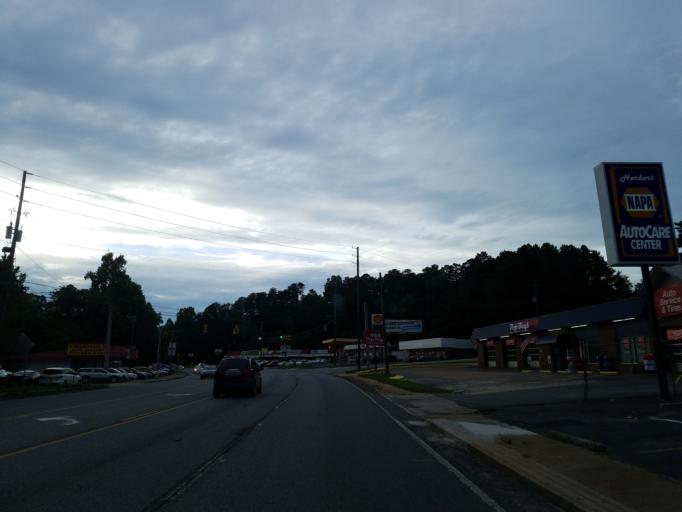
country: US
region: Georgia
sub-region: Forsyth County
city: Cumming
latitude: 34.2109
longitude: -84.1440
